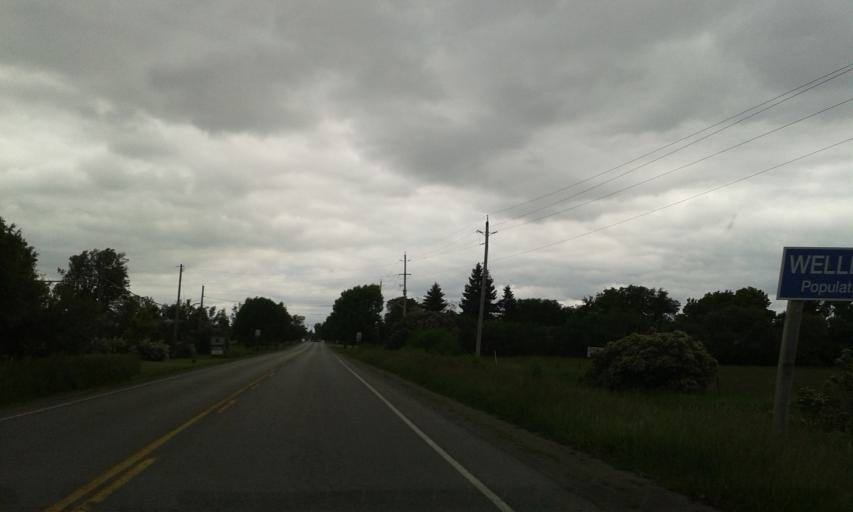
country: CA
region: Ontario
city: Prince Edward
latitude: 43.9460
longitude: -77.3735
